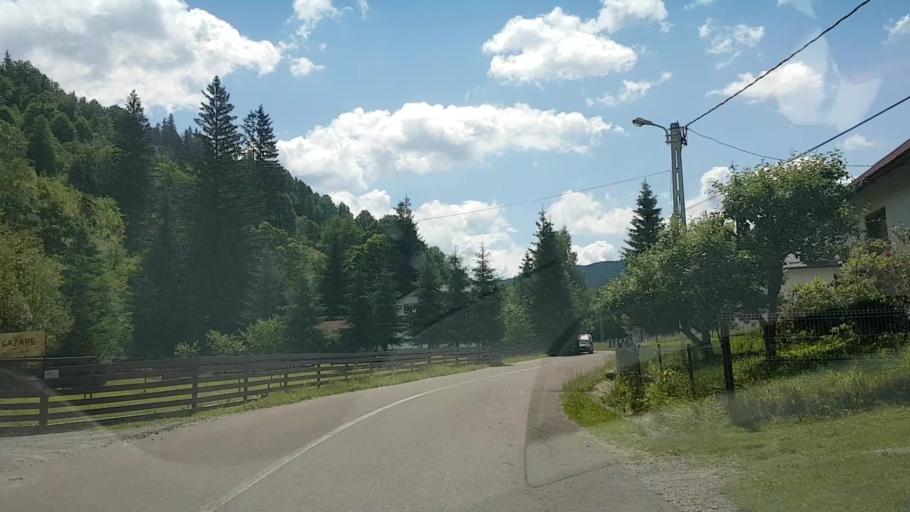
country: RO
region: Suceava
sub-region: Comuna Pojorata
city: Pojorata
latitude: 47.4942
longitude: 25.4835
